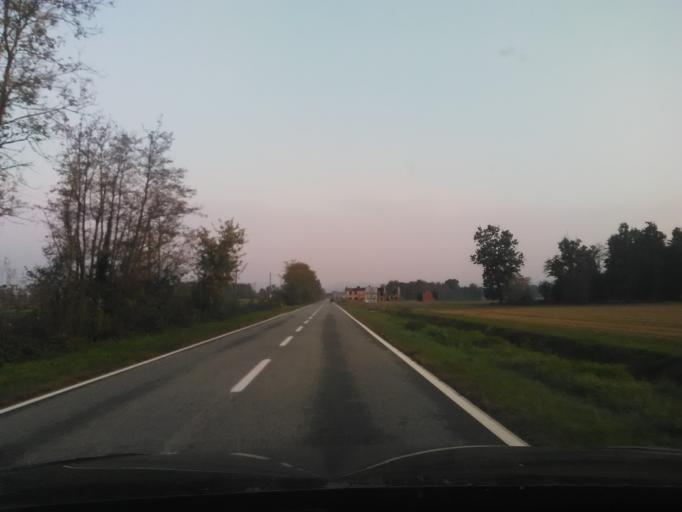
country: IT
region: Piedmont
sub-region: Provincia di Vercelli
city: Rovasenda
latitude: 45.5435
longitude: 8.3023
